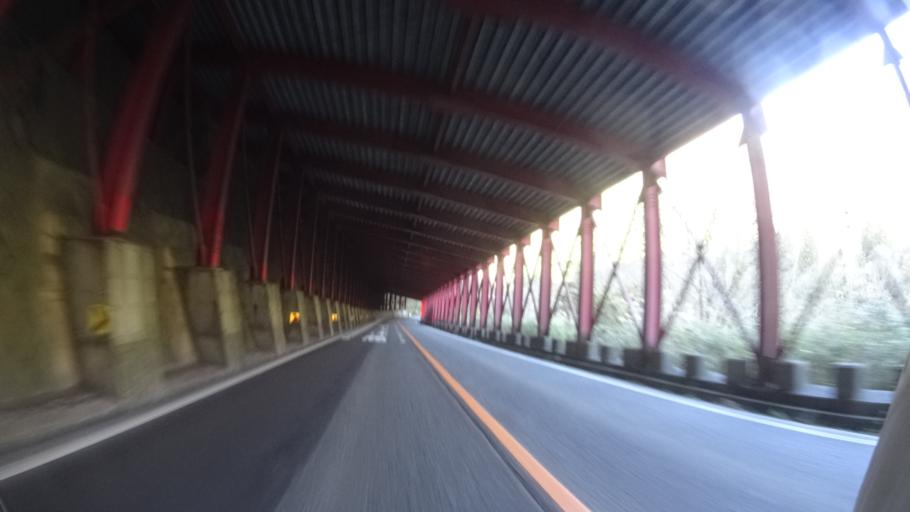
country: JP
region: Fukui
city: Ono
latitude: 35.9465
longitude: 136.6393
